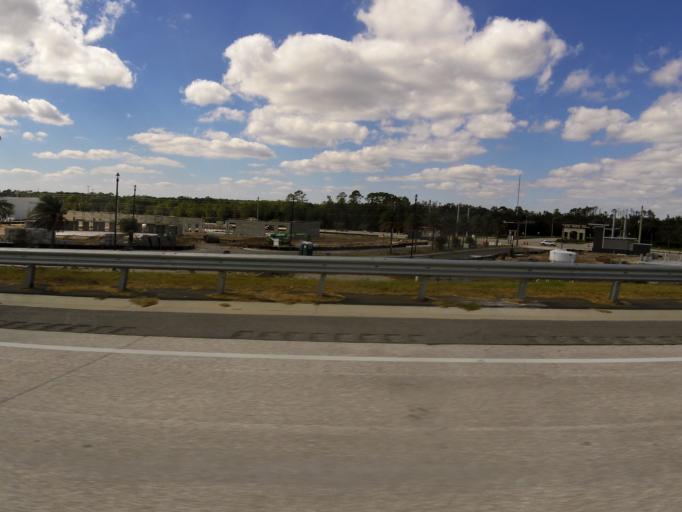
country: US
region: Florida
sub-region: Saint Johns County
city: Fruit Cove
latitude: 30.1024
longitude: -81.5170
